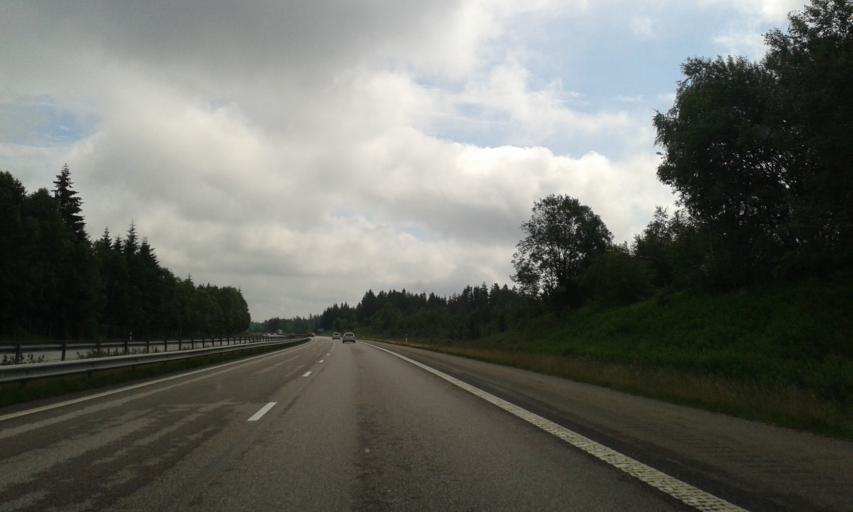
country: SE
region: Vaestra Goetaland
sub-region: Boras Kommun
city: Sandared
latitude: 57.6809
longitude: 12.7250
